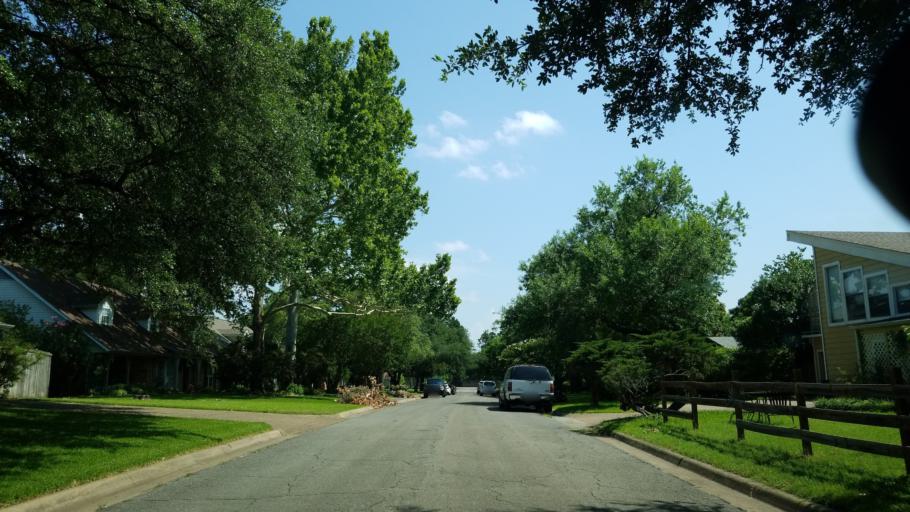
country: US
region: Texas
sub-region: Dallas County
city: Farmers Branch
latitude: 32.8887
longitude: -96.8678
